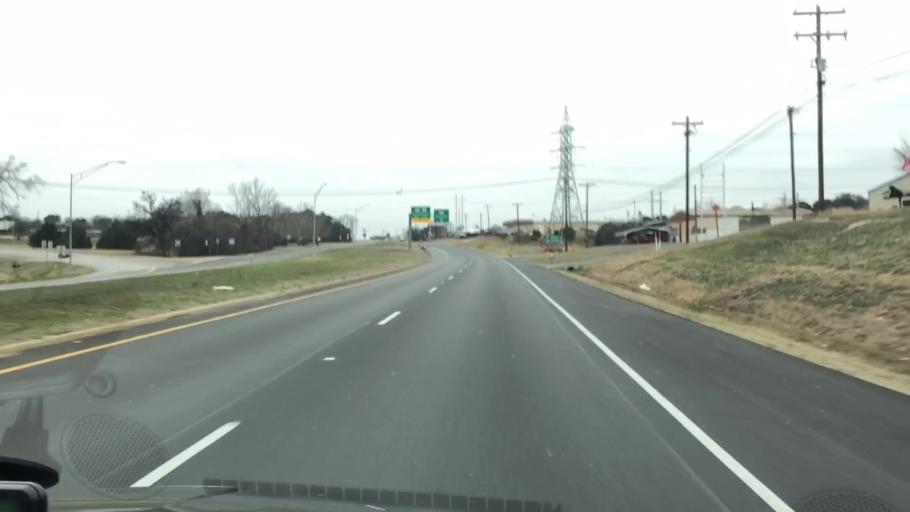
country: US
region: Texas
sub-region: Lampasas County
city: Lampasas
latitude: 31.0825
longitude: -98.1869
